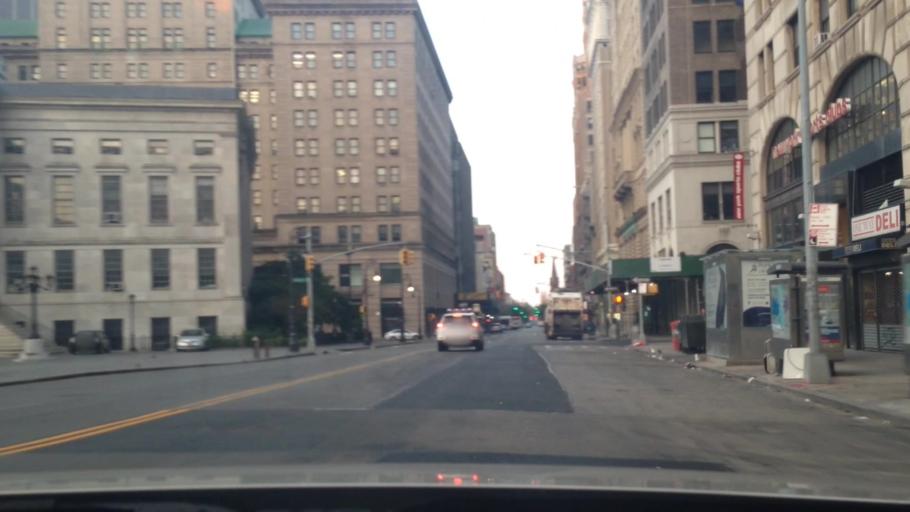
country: US
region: New York
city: New York City
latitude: 40.6936
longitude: -73.9905
